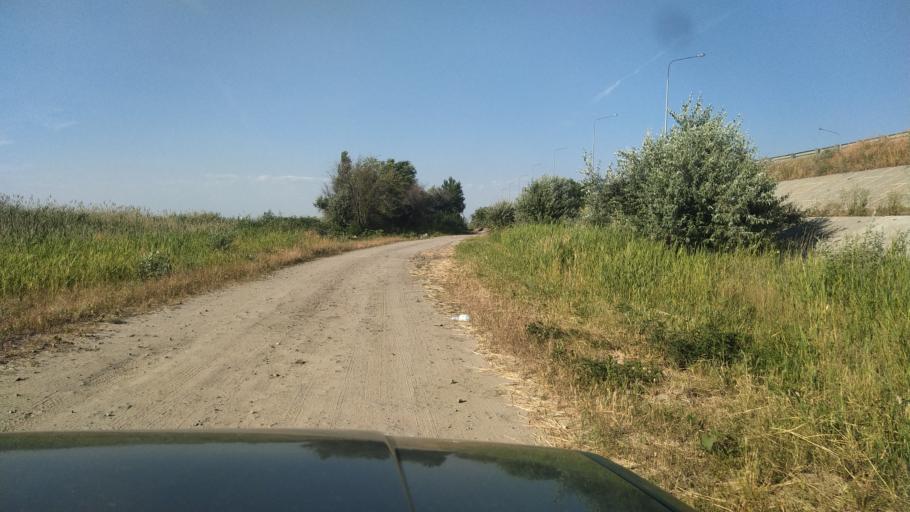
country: RU
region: Rostov
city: Bataysk
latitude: 47.1231
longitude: 39.6617
